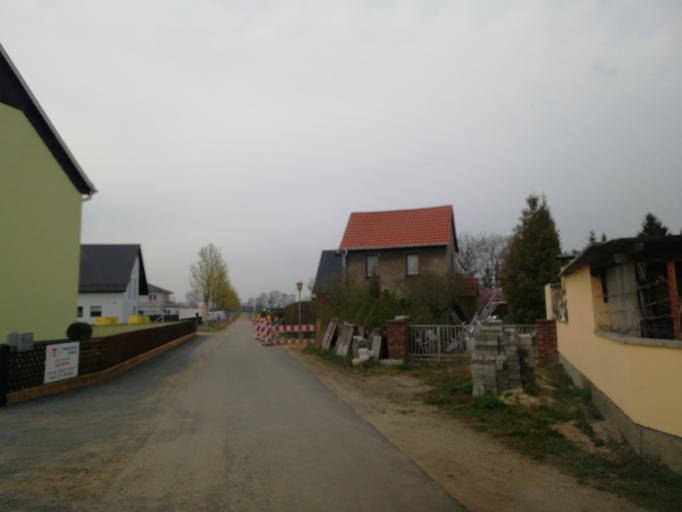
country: DE
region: Brandenburg
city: Elsterwerda
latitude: 51.4293
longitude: 13.4899
